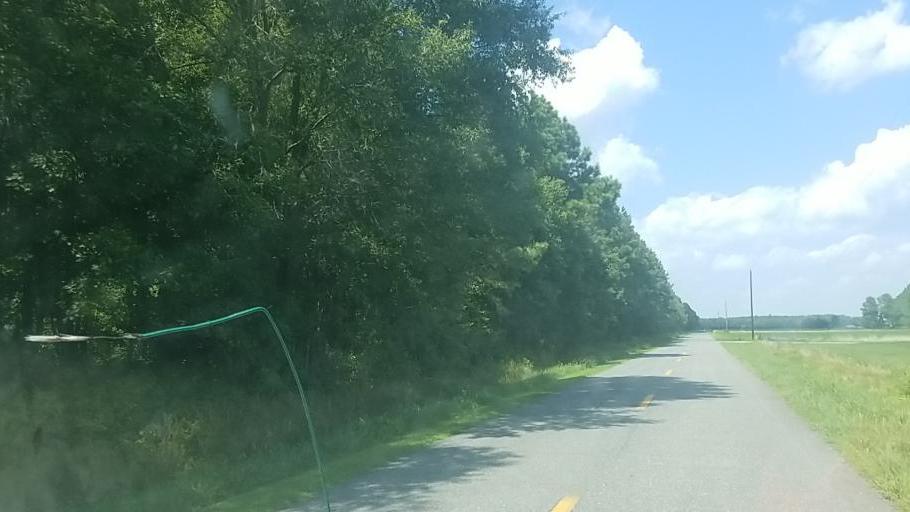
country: US
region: Maryland
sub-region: Wicomico County
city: Hebron
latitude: 38.4594
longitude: -75.8471
